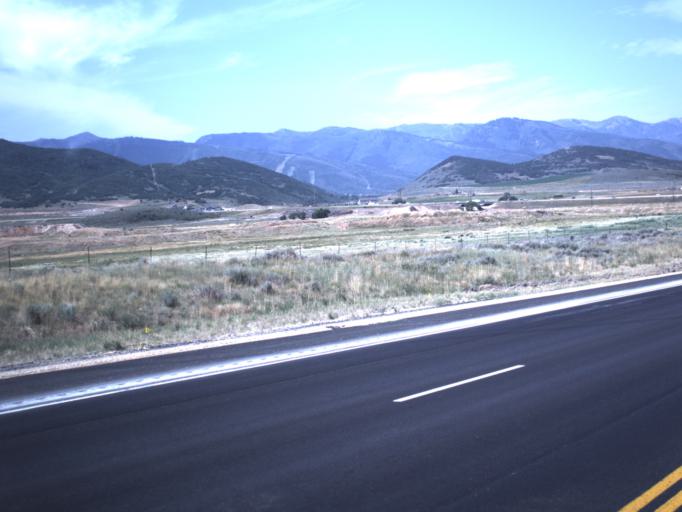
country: US
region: Utah
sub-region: Summit County
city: Park City
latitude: 40.6814
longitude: -111.4481
